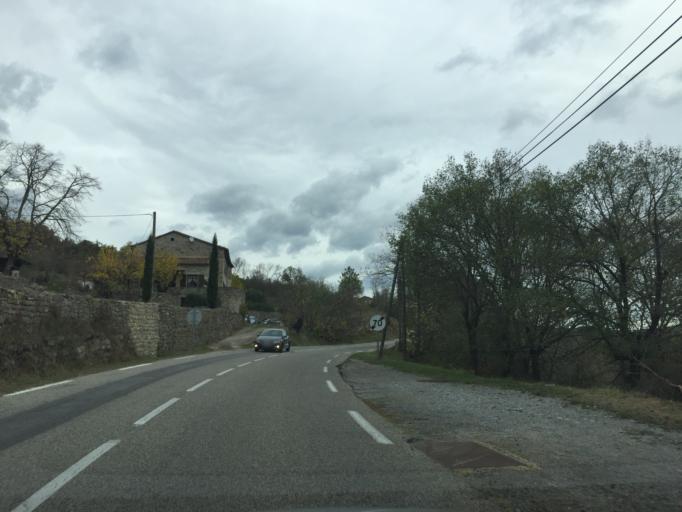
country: FR
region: Rhone-Alpes
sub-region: Departement de l'Ardeche
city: Les Vans
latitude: 44.4182
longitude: 4.1755
